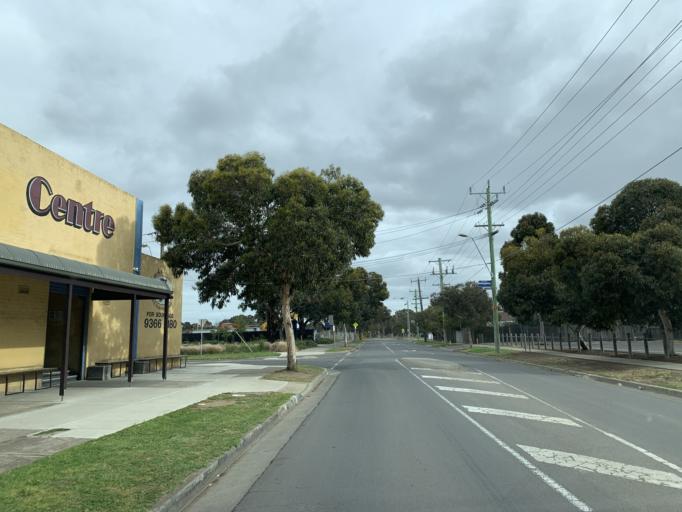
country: AU
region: Victoria
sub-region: Brimbank
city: St Albans
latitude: -37.7470
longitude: 144.7996
